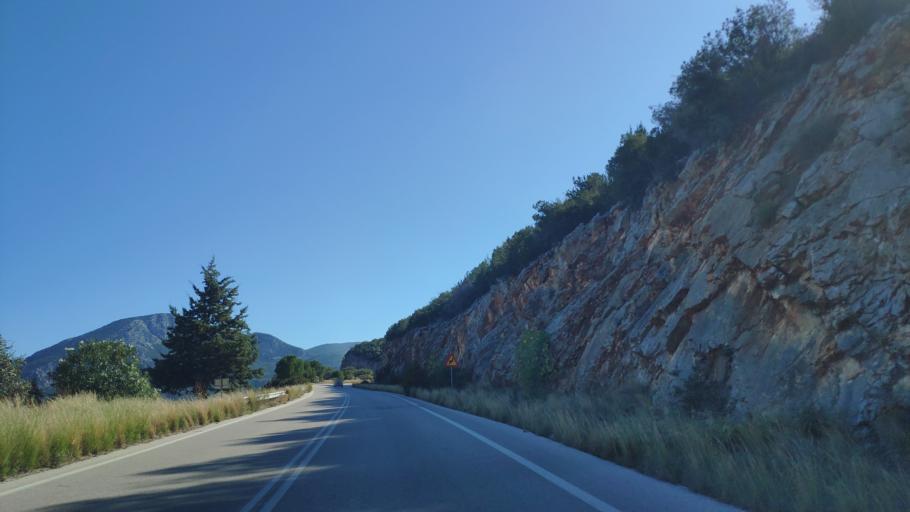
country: GR
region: Peloponnese
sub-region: Nomos Argolidos
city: Palaia Epidavros
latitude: 37.6268
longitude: 23.1438
